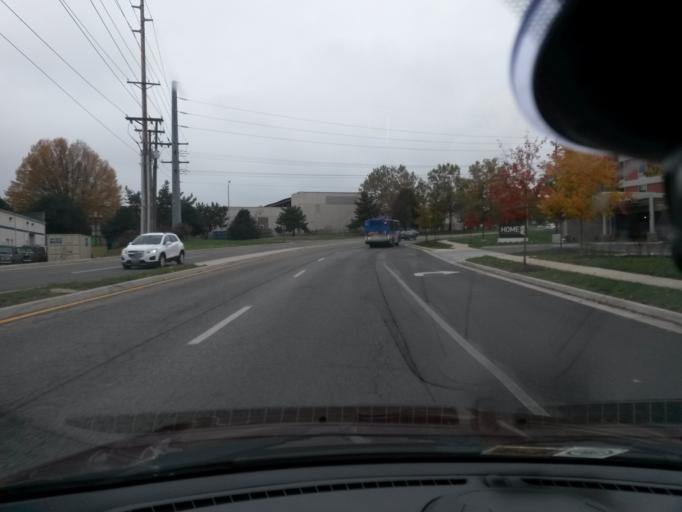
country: US
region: Virginia
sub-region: City of Roanoke
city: Roanoke
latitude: 37.3053
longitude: -79.9608
